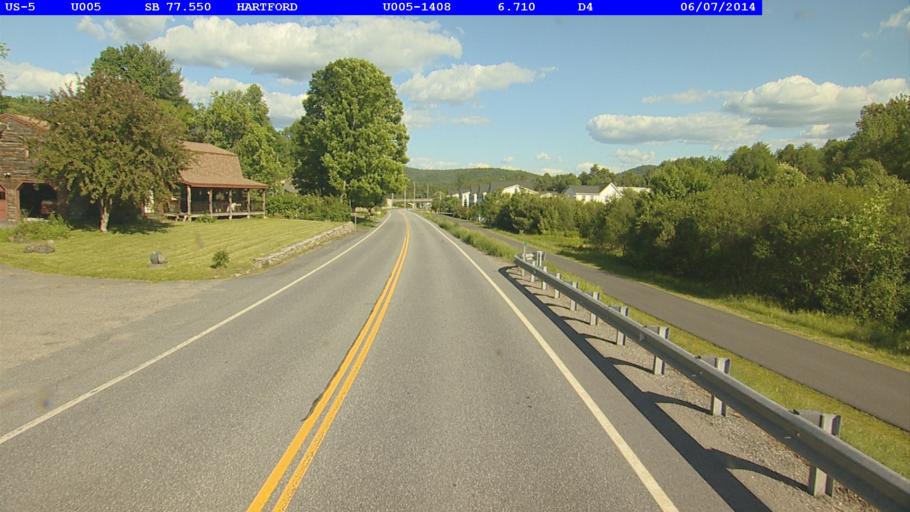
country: US
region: Vermont
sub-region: Windsor County
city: Wilder
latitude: 43.6845
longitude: -72.3202
